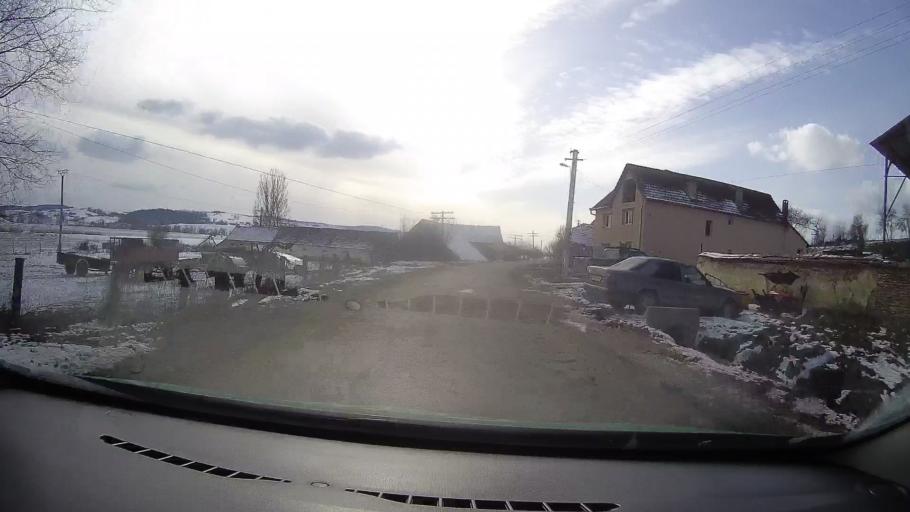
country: RO
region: Sibiu
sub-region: Comuna Bradeni
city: Bradeni
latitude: 46.0545
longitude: 24.7832
